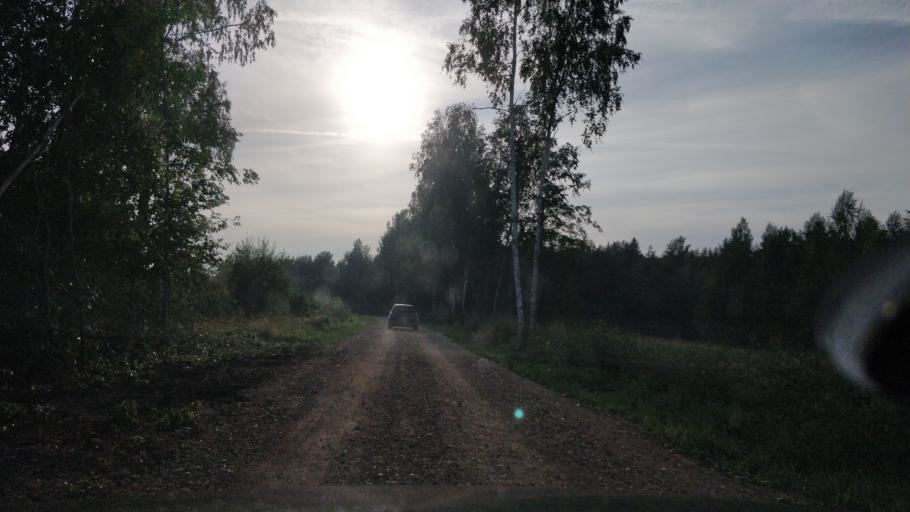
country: LV
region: Sigulda
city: Sigulda
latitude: 57.1009
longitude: 24.7868
